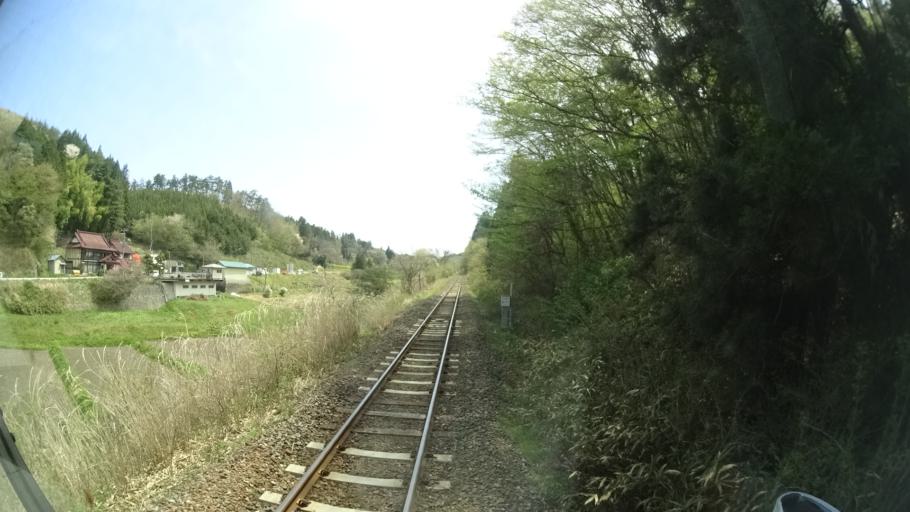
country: JP
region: Iwate
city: Ichinoseki
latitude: 38.9373
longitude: 141.3970
